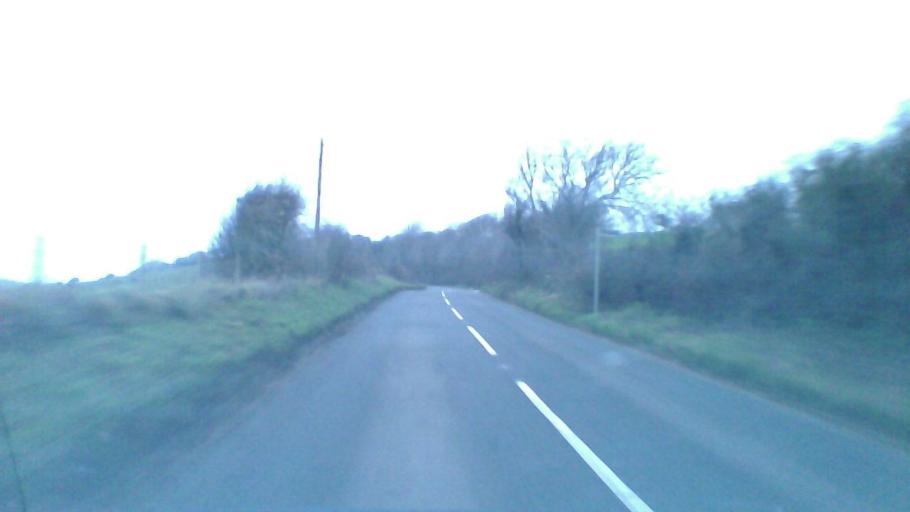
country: GB
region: England
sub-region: Isle of Wight
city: Newchurch
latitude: 50.6828
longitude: -1.1859
